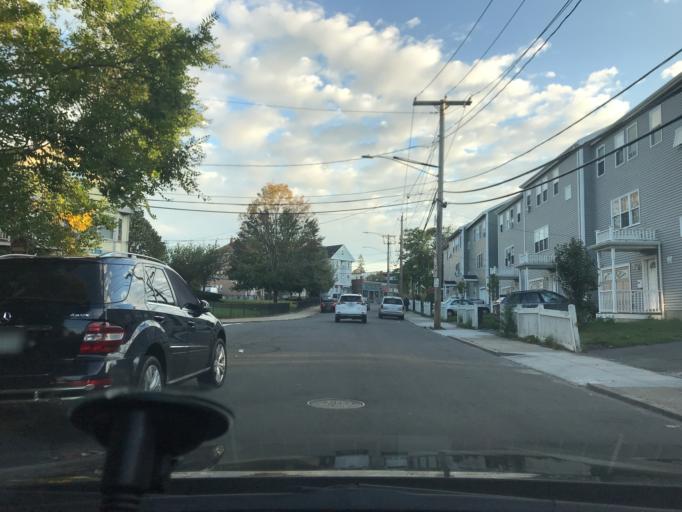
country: US
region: Massachusetts
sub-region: Suffolk County
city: Jamaica Plain
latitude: 42.3018
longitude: -71.0795
